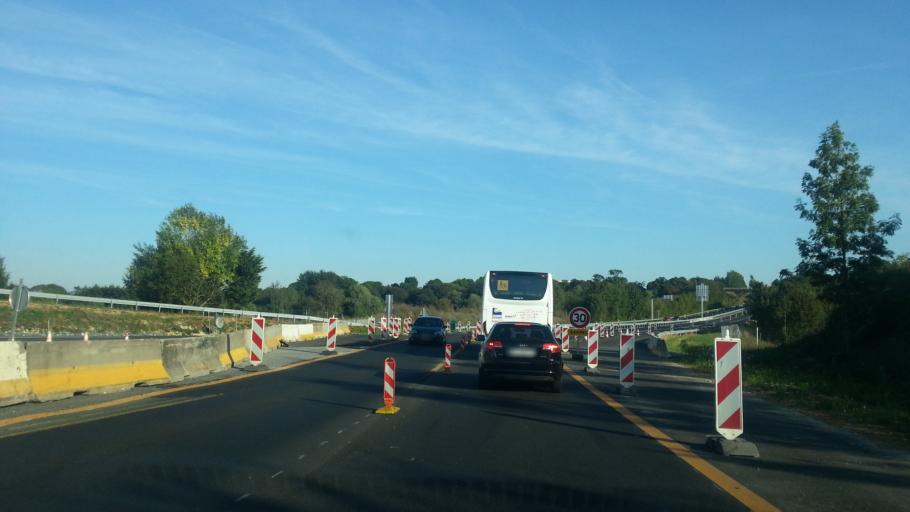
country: FR
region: Picardie
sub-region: Departement de l'Oise
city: Tille
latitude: 49.4597
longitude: 2.0879
